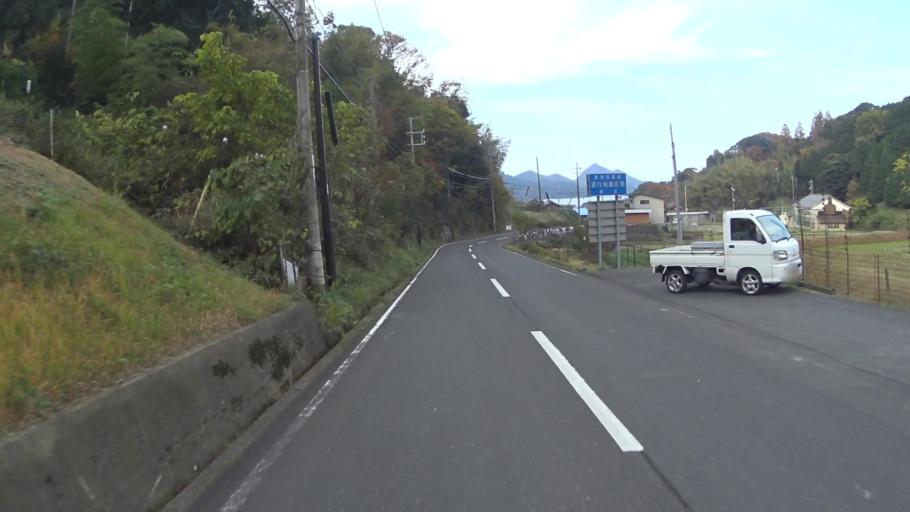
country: JP
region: Kyoto
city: Maizuru
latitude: 35.5630
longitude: 135.4542
